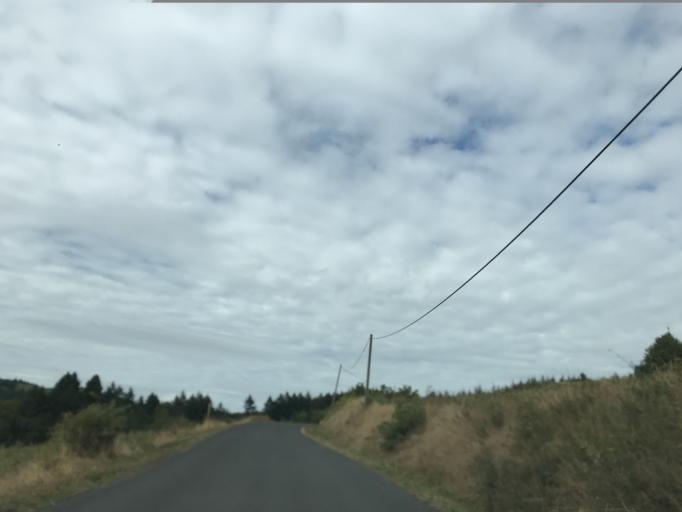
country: FR
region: Auvergne
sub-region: Departement du Puy-de-Dome
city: Celles-sur-Durolle
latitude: 45.8290
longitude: 3.6320
